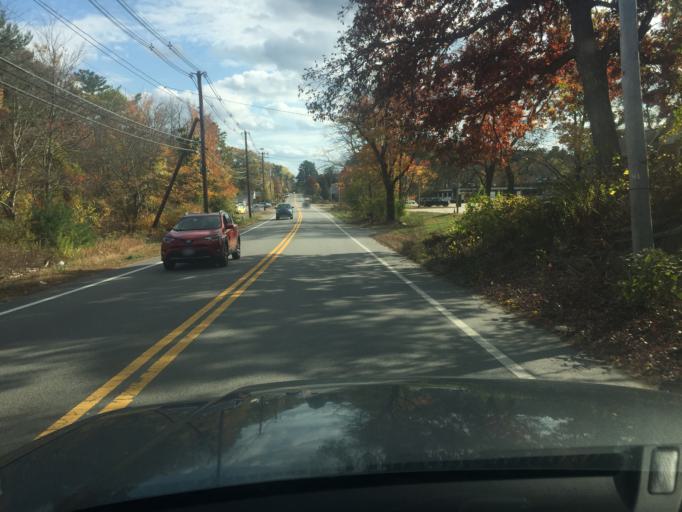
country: US
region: Massachusetts
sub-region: Worcester County
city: Milford
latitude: 42.1184
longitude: -71.5125
